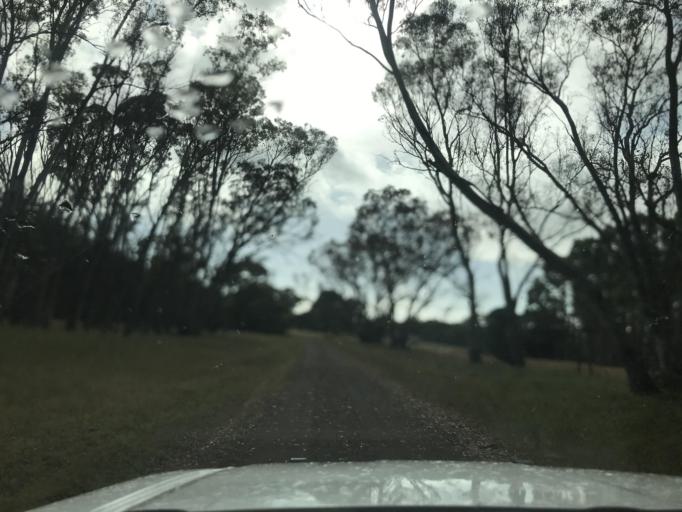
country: AU
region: South Australia
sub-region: Wattle Range
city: Penola
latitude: -37.2207
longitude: 141.2894
